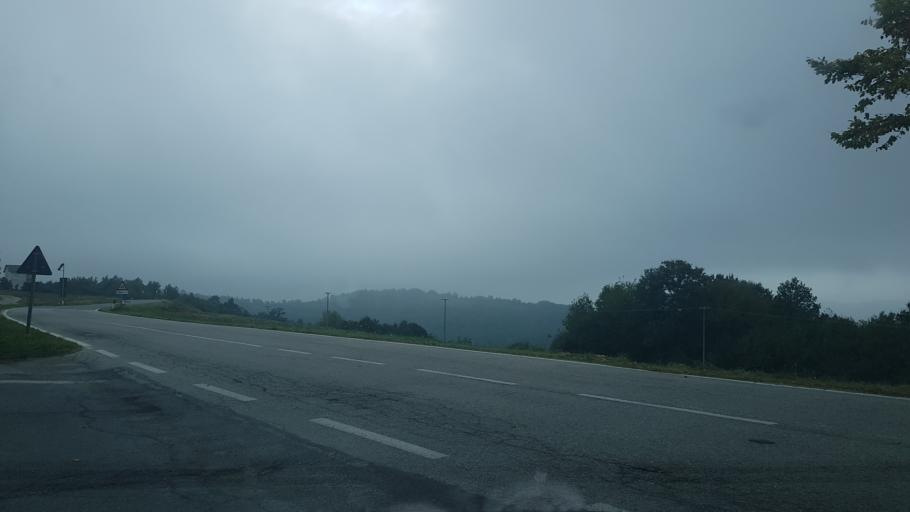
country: IT
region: Piedmont
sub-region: Provincia di Cuneo
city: Paroldo
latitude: 44.4240
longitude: 8.0954
